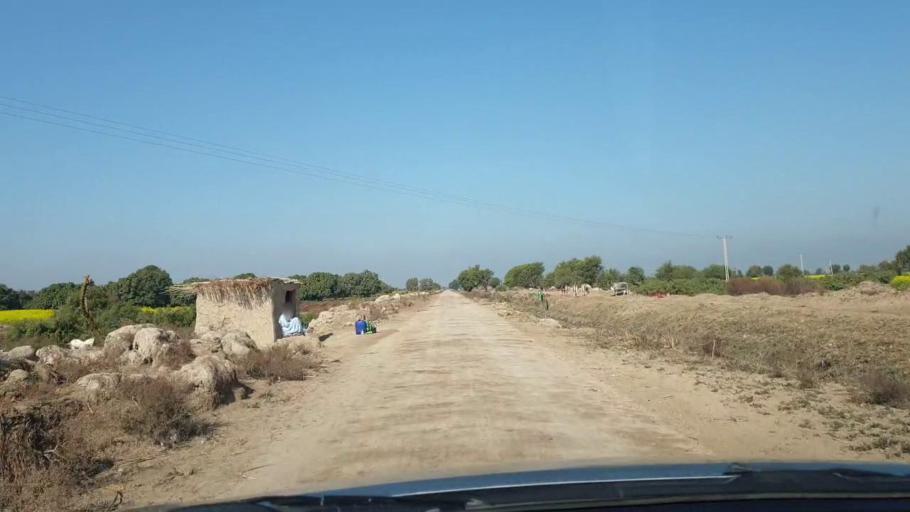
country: PK
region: Sindh
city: Jhol
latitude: 25.8818
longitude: 68.9020
